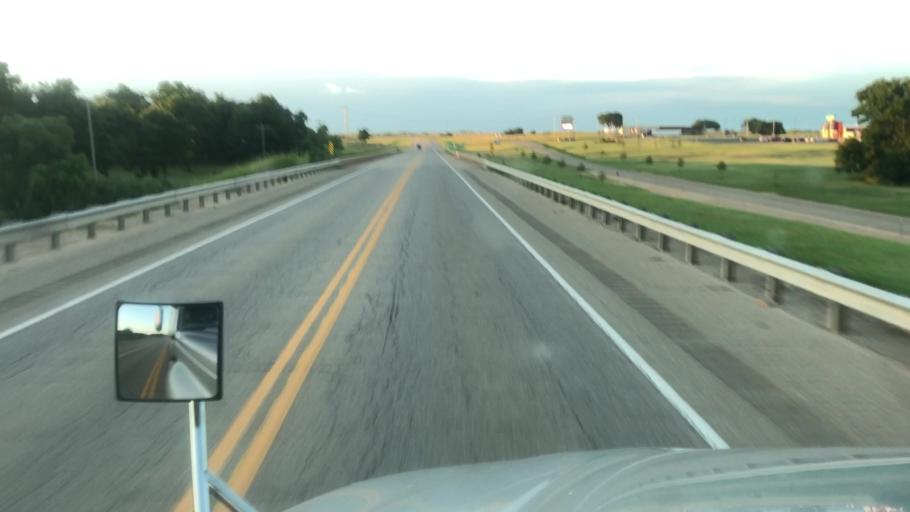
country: US
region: Oklahoma
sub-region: Osage County
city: McCord
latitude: 36.4959
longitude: -97.0737
